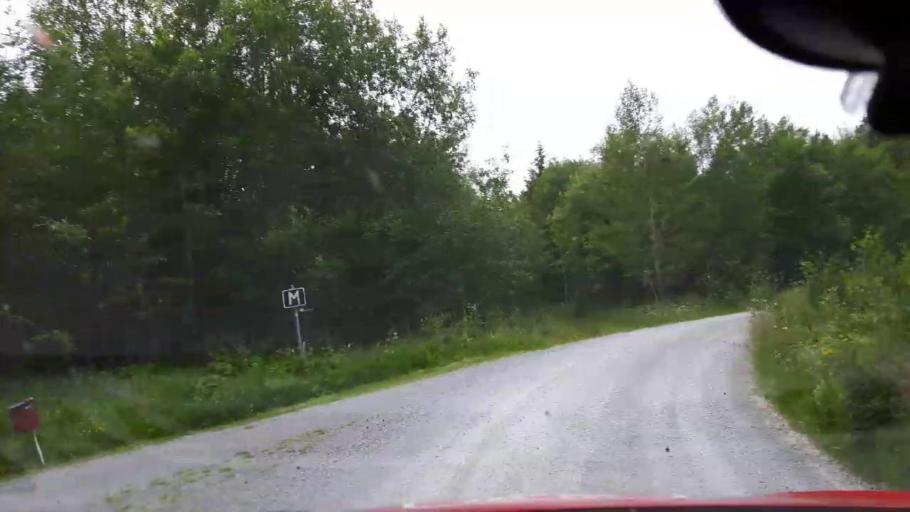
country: SE
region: Jaemtland
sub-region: OEstersunds Kommun
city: Brunflo
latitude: 63.0335
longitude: 14.9303
